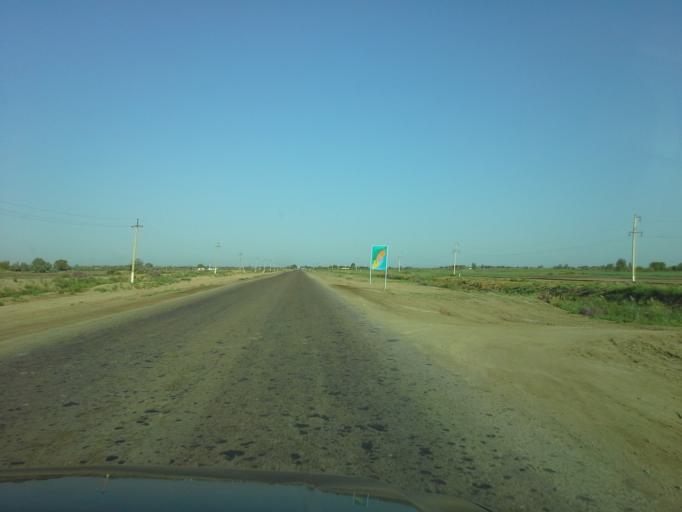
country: UZ
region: Karakalpakstan
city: Khujayli
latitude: 42.2235
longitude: 59.4826
